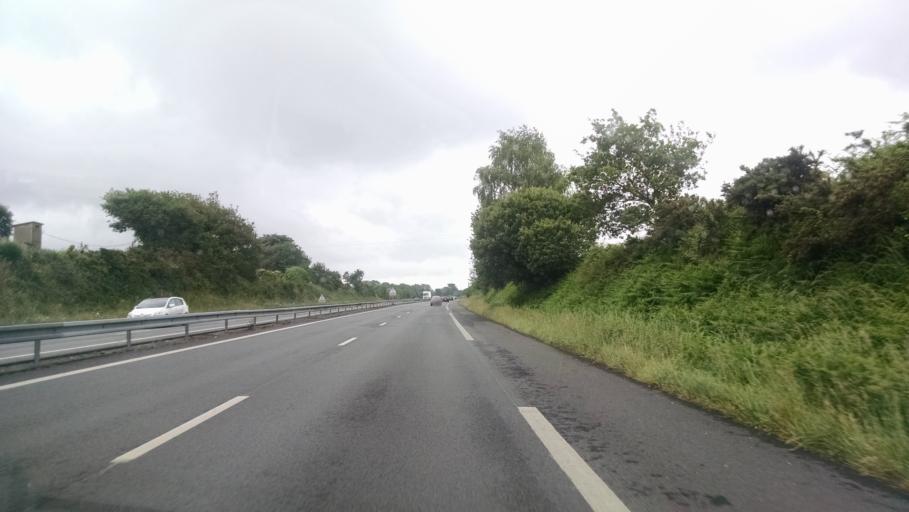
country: FR
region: Brittany
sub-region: Departement du Morbihan
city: Brech
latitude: 47.7003
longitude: -3.0408
